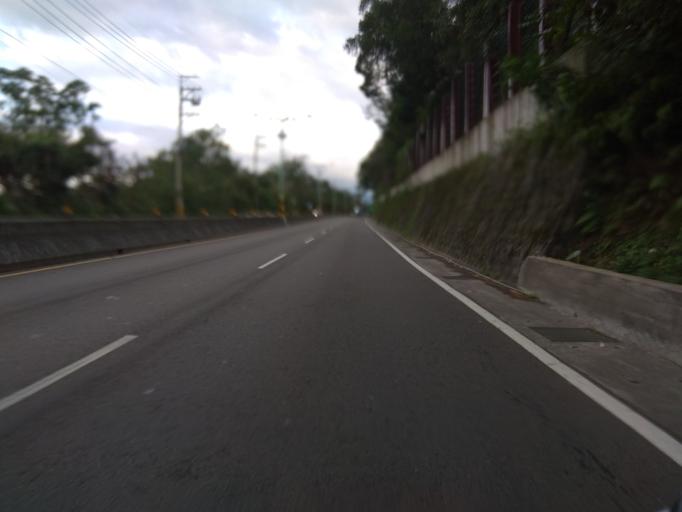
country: TW
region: Taiwan
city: Daxi
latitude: 24.8469
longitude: 121.2085
